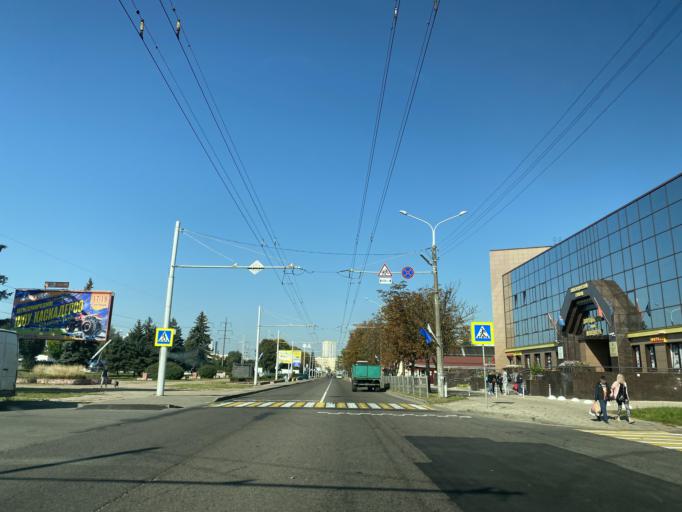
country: BY
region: Minsk
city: Borovlyany
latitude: 53.9462
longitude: 27.6299
